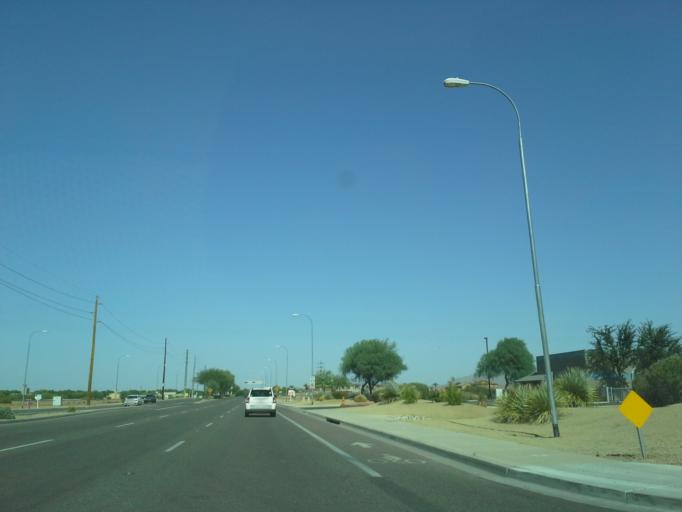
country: US
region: Arizona
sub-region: Maricopa County
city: Sun Lakes
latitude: 33.2185
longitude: -111.8404
